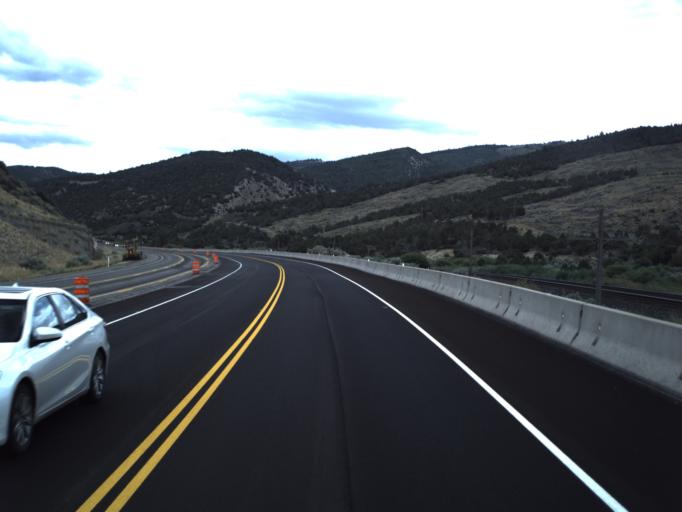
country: US
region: Utah
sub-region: Utah County
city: Mapleton
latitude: 39.9559
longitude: -111.2995
